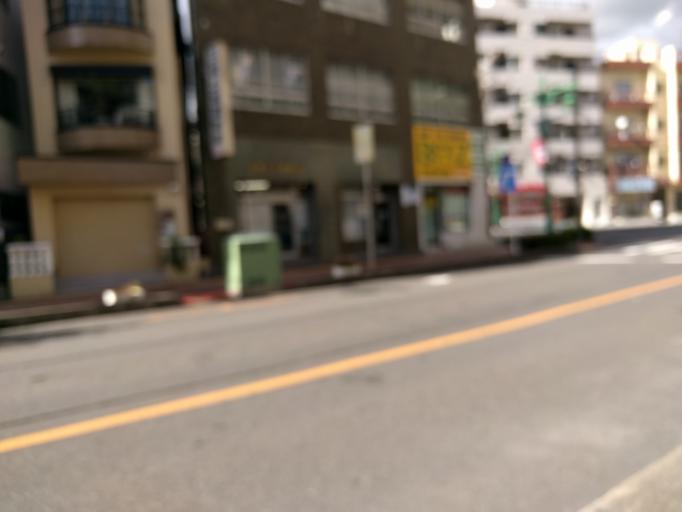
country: JP
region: Saitama
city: Shimotoda
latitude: 35.8298
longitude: 139.6936
